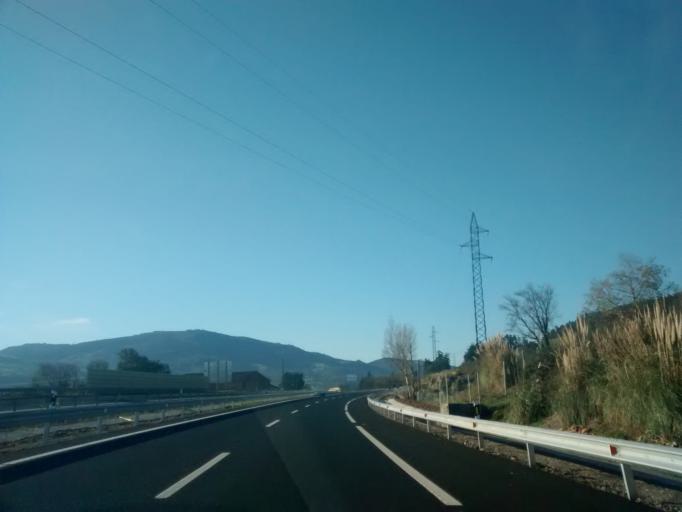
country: ES
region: Cantabria
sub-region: Provincia de Cantabria
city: Santa Maria de Cayon
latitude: 43.3277
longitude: -3.8543
